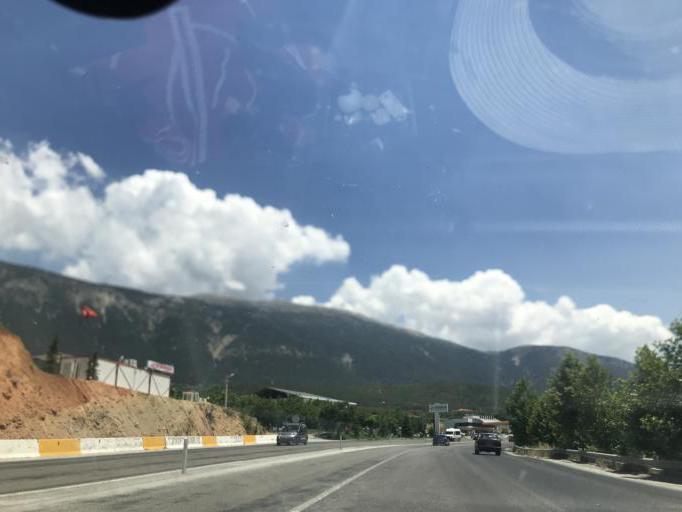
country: TR
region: Denizli
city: Honaz
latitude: 37.6856
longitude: 29.2197
